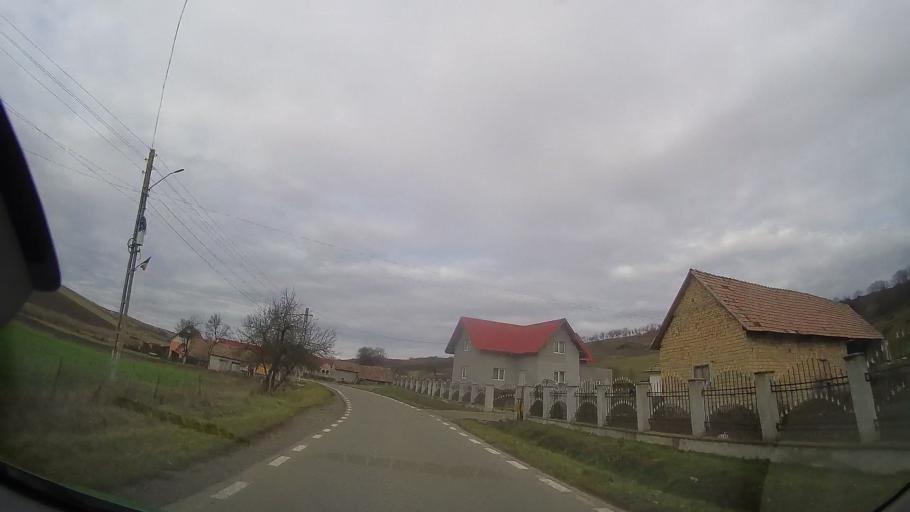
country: RO
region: Mures
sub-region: Comuna Cozma
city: Cozma
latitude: 46.8136
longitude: 24.4981
